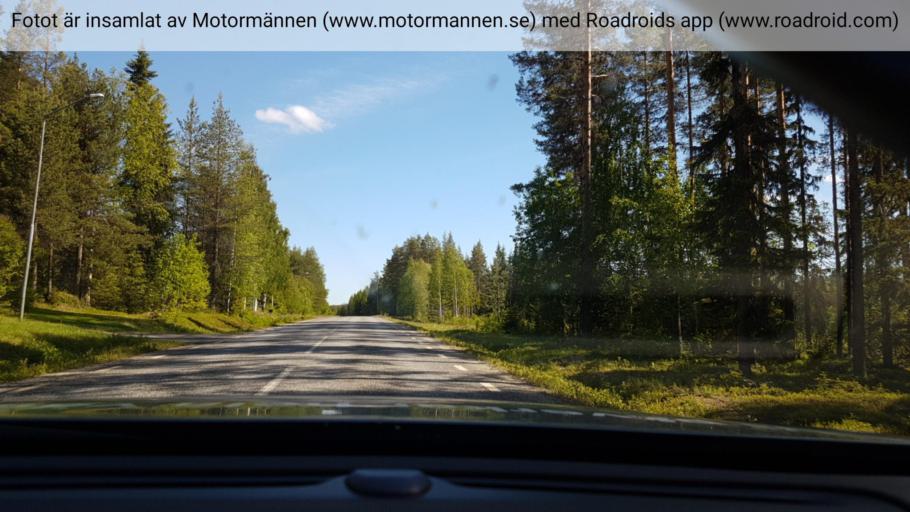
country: SE
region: Vaesterbotten
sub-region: Lycksele Kommun
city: Lycksele
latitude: 64.5920
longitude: 18.5548
